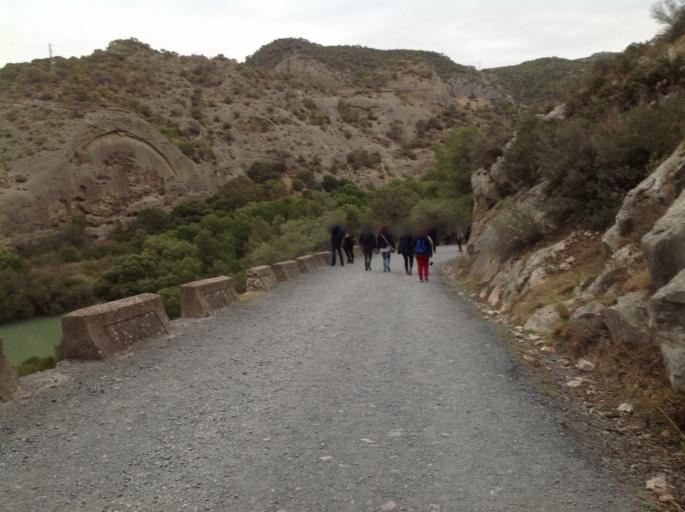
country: ES
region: Andalusia
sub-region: Provincia de Malaga
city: Ardales
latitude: 36.9295
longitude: -4.7927
